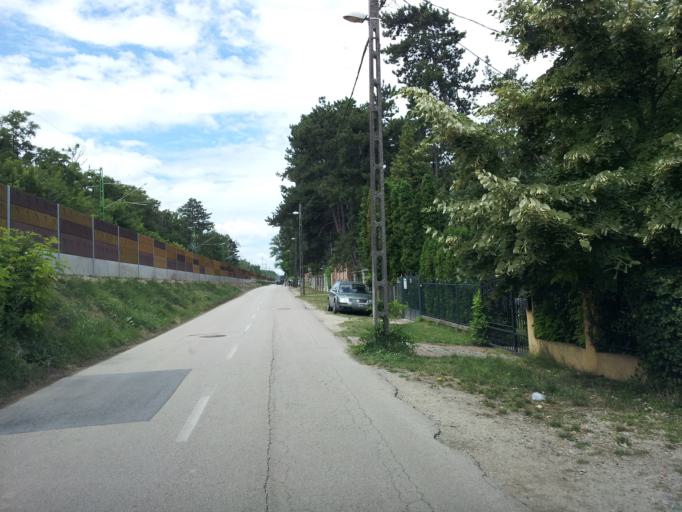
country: HU
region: Somogy
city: Balatonszabadi
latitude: 46.9390
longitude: 18.1276
